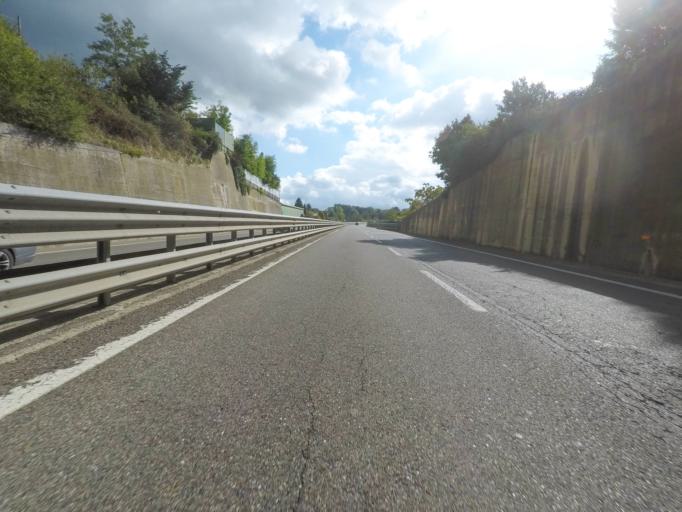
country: IT
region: Tuscany
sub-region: Provincia di Siena
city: Rapolano Terme
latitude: 43.3040
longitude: 11.5939
